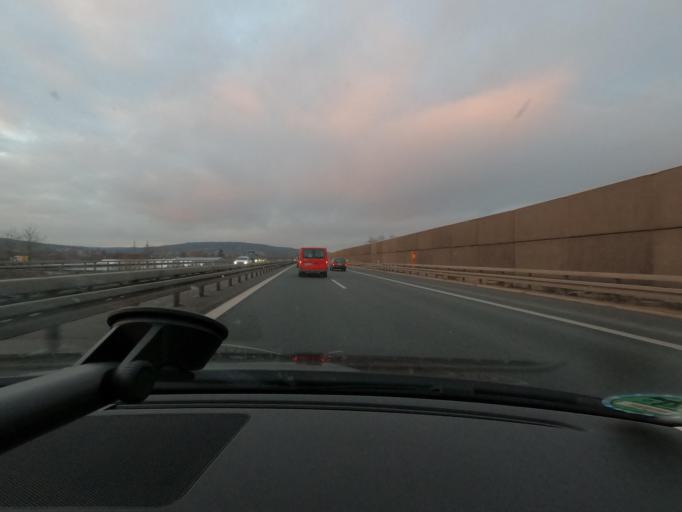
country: DE
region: Bavaria
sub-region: Upper Franconia
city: Forchheim
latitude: 49.7076
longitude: 11.0566
